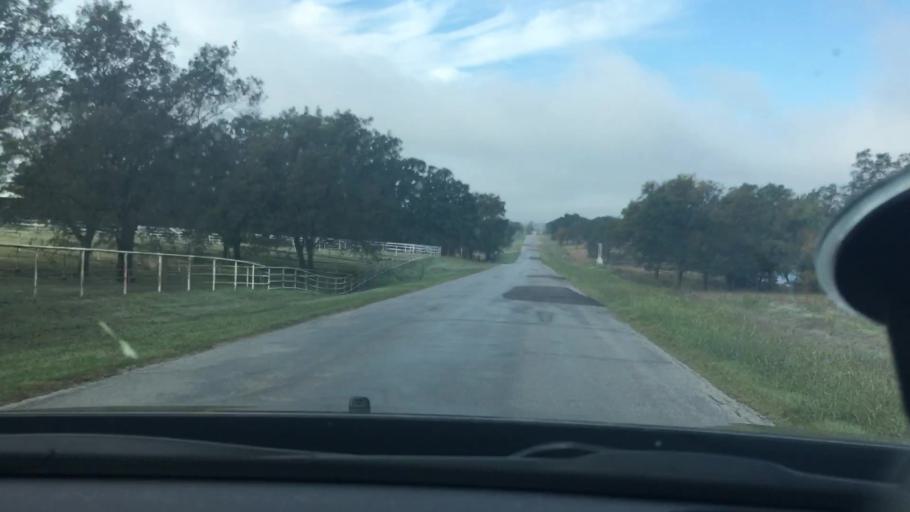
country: US
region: Oklahoma
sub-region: Murray County
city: Sulphur
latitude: 34.6223
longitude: -96.9592
